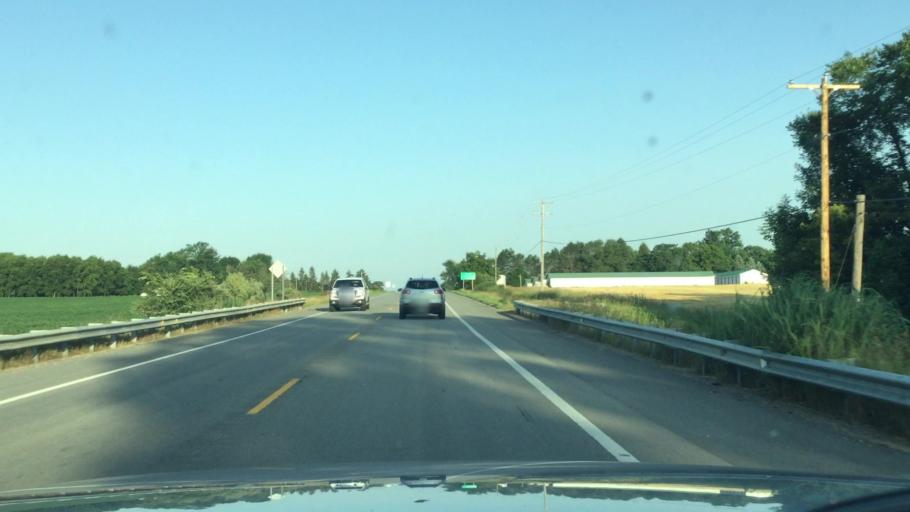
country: US
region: Michigan
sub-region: Gratiot County
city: Ithaca
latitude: 43.1761
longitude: -84.6744
